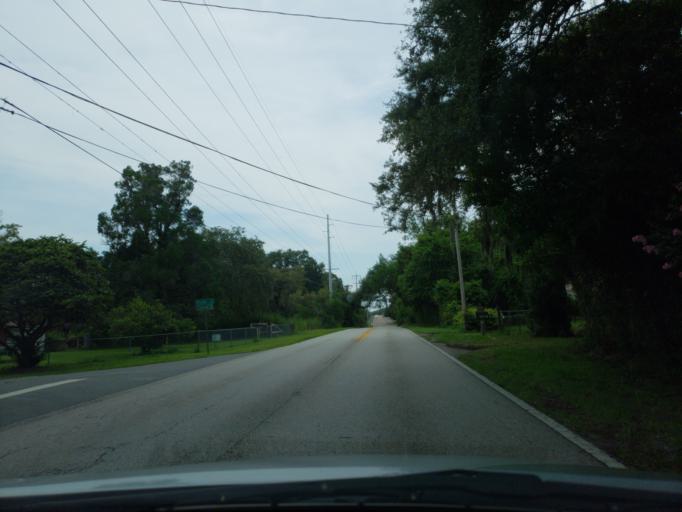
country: US
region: Florida
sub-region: Hillsborough County
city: University
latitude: 28.1120
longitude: -82.4307
